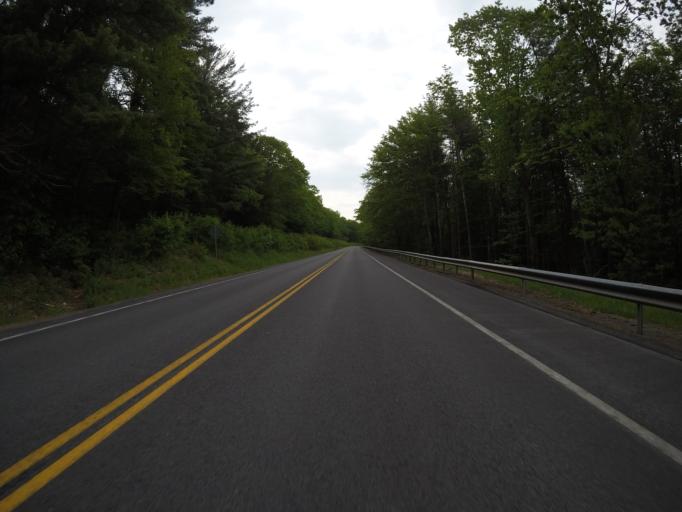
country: US
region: New York
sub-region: Sullivan County
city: Livingston Manor
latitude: 42.0608
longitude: -74.9250
